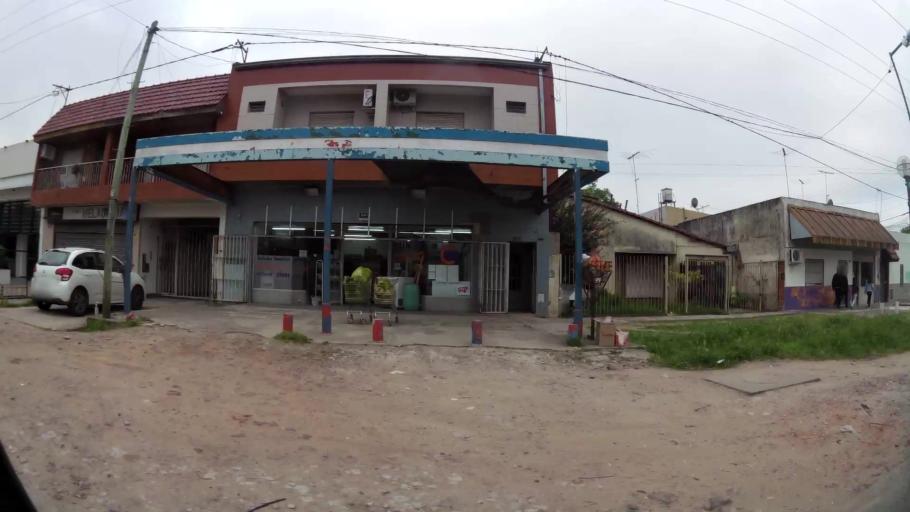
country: AR
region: Buenos Aires
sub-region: Partido de La Plata
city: La Plata
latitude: -34.9316
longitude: -57.9905
